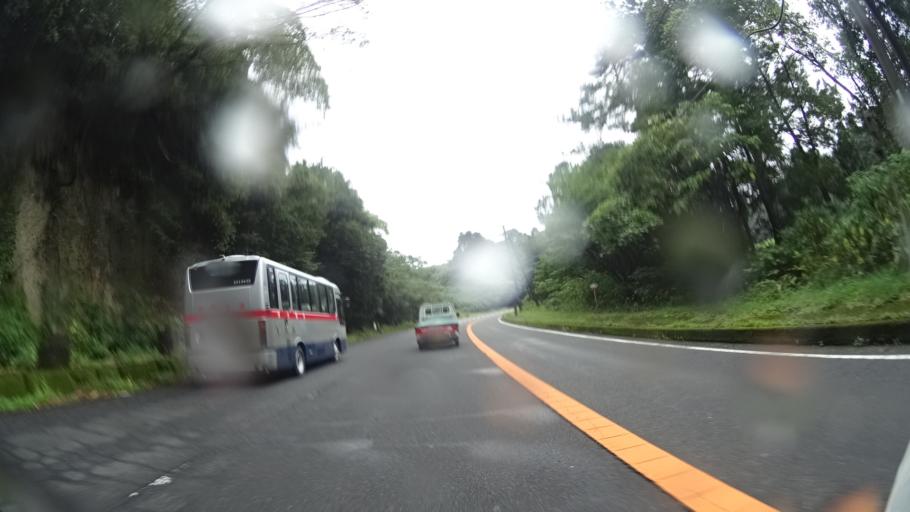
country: JP
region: Kagoshima
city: Kajiki
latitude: 31.7757
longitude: 130.6692
